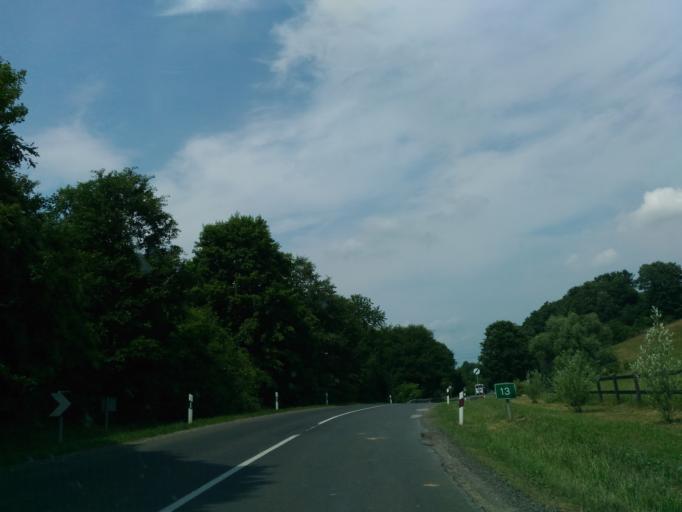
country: HU
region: Baranya
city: Komlo
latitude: 46.1713
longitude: 18.2125
